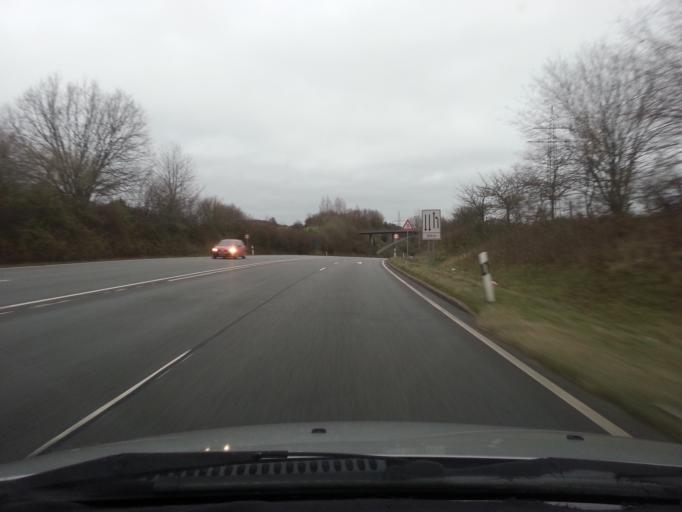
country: DE
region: Hesse
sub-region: Regierungsbezirk Darmstadt
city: Birkenau
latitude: 49.5802
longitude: 8.7087
